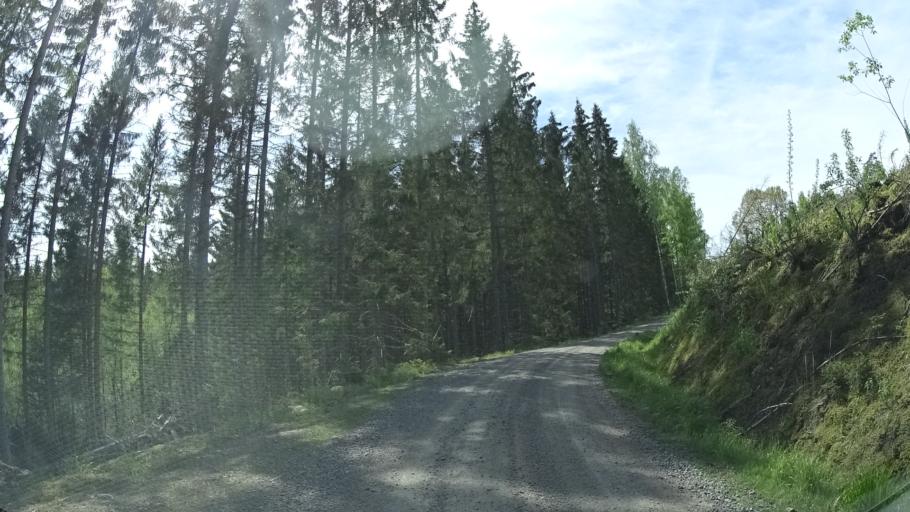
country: SE
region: OEstergoetland
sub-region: Finspangs Kommun
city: Finspang
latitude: 58.7852
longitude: 15.8468
